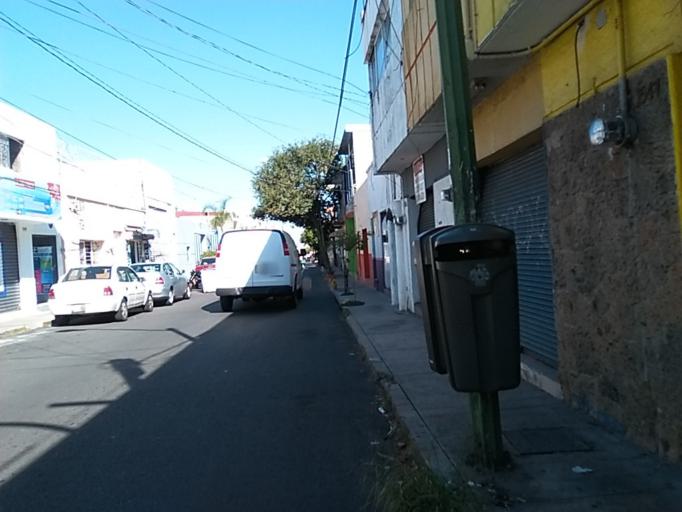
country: MX
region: Jalisco
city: Guadalajara
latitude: 20.6856
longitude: -103.3680
